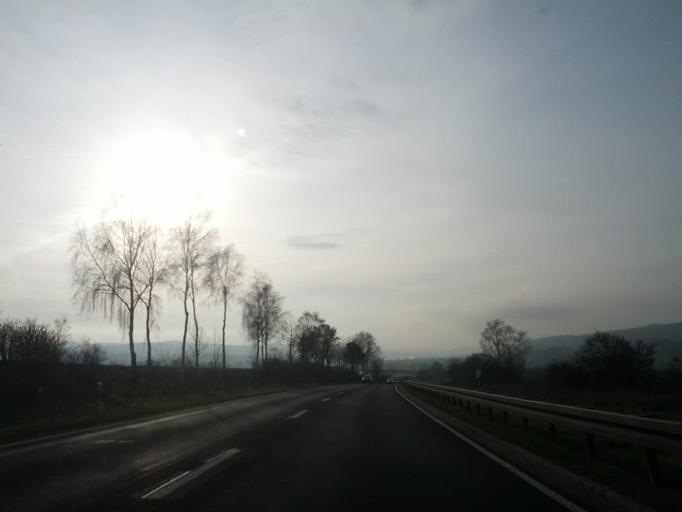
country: DE
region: Thuringia
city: Fambach
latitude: 50.7510
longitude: 10.3567
